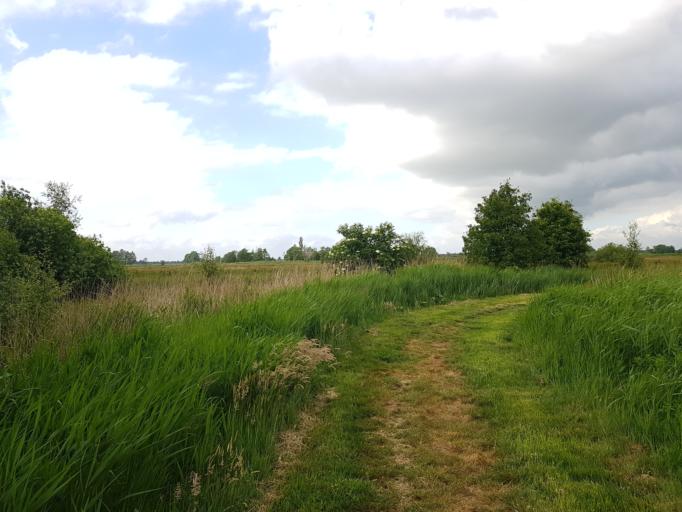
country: NL
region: Friesland
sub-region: Gemeente Smallingerland
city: Oudega
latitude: 53.0886
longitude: 5.9641
